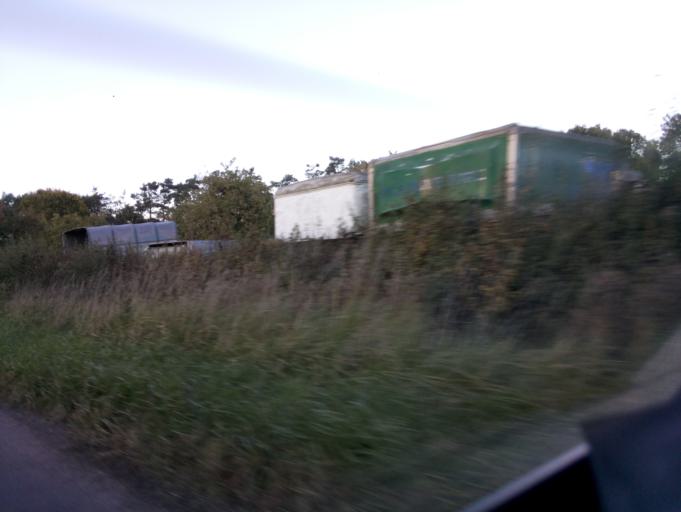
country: GB
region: England
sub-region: Worcestershire
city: Upton upon Severn
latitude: 52.0085
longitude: -2.2779
